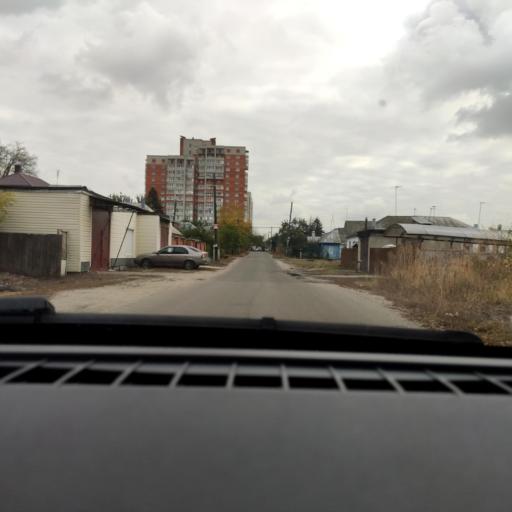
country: RU
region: Voronezj
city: Voronezh
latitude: 51.6688
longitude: 39.2560
